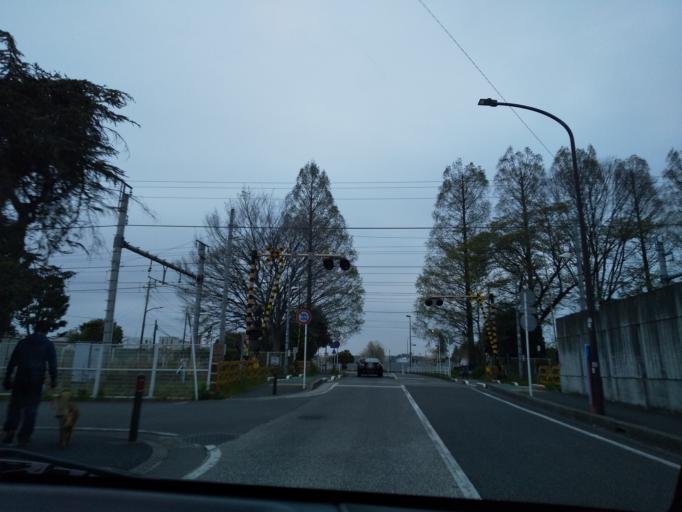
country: JP
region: Tokyo
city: Hachioji
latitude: 35.5832
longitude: 139.3668
